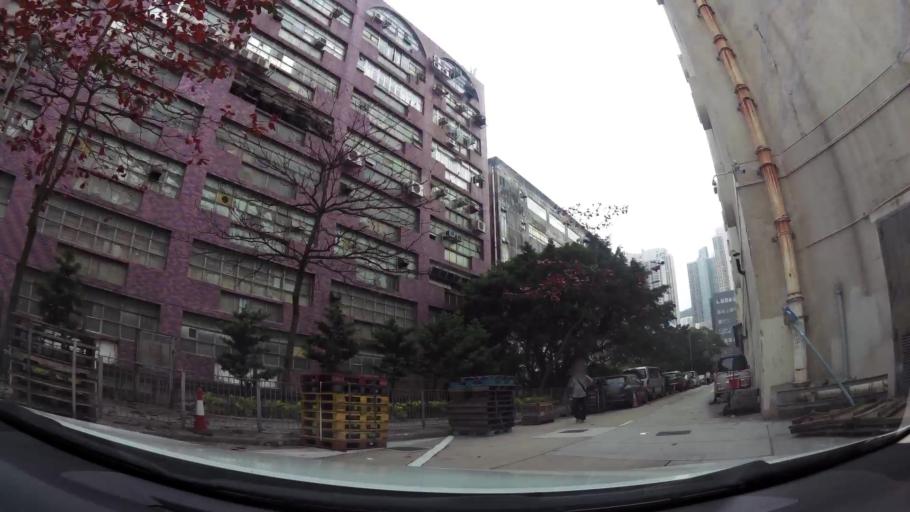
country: HK
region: Kowloon City
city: Kowloon
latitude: 22.2949
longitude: 114.2356
